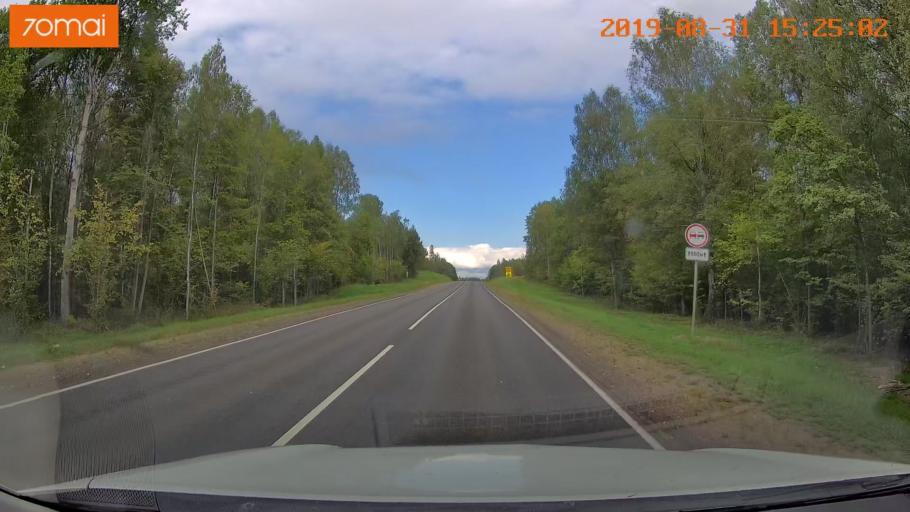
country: RU
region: Kaluga
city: Baryatino
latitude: 54.5358
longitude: 34.5135
